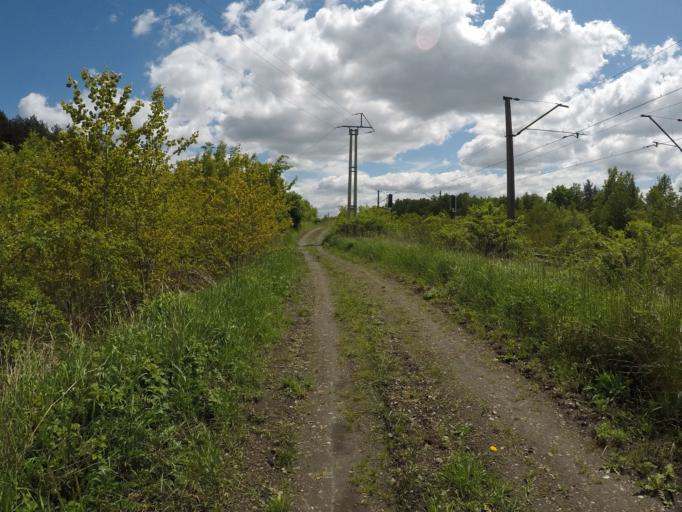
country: PL
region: Swietokrzyskie
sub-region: Powiat kielecki
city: Kostomloty Pierwsze
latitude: 50.9270
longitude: 20.6049
